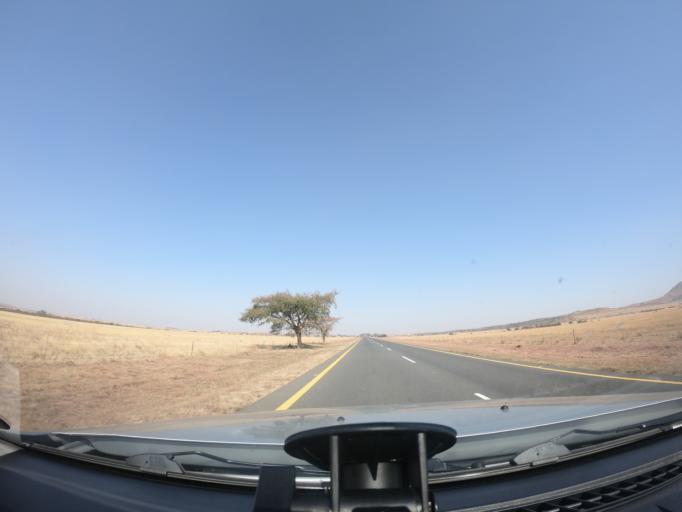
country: ZA
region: KwaZulu-Natal
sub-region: uThukela District Municipality
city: Ekuvukeni
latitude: -28.3850
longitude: 29.9403
